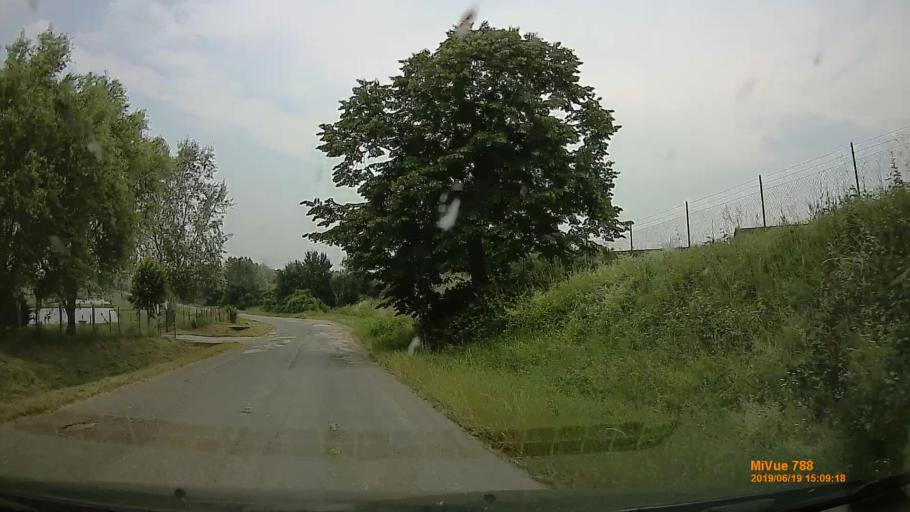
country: HU
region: Baranya
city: Szigetvar
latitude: 46.0850
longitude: 17.8015
